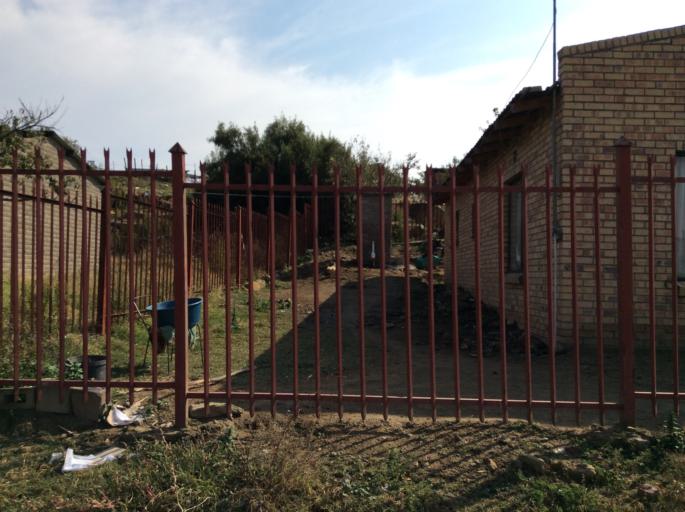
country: LS
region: Mafeteng
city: Mafeteng
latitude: -29.7225
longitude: 27.0361
